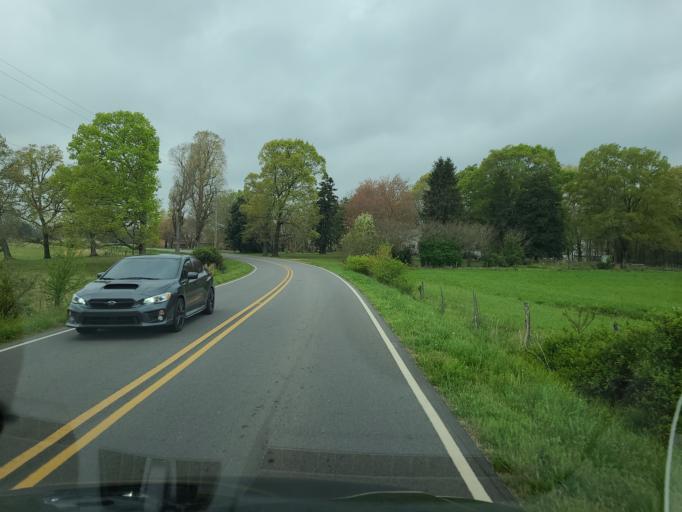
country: US
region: North Carolina
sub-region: Gaston County
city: Cherryville
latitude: 35.4340
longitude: -81.4281
